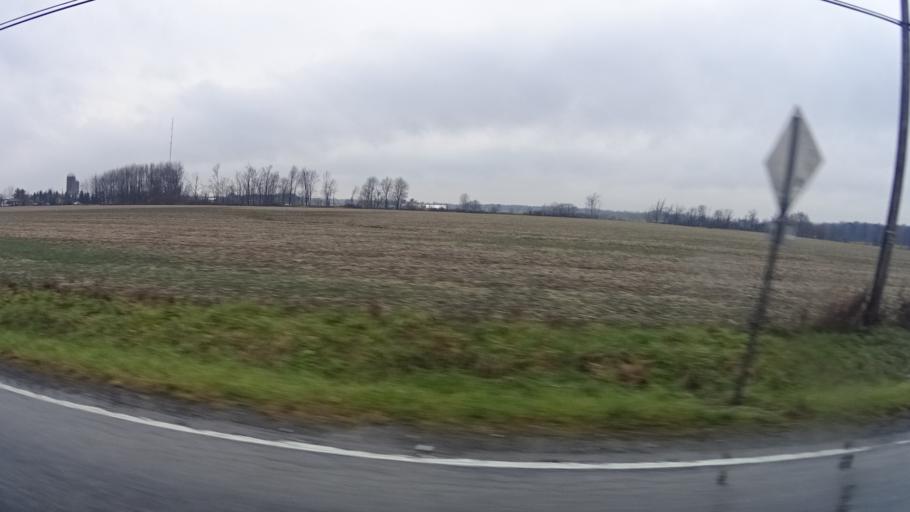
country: US
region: Ohio
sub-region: Lorain County
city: Lagrange
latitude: 41.2391
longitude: -82.1391
